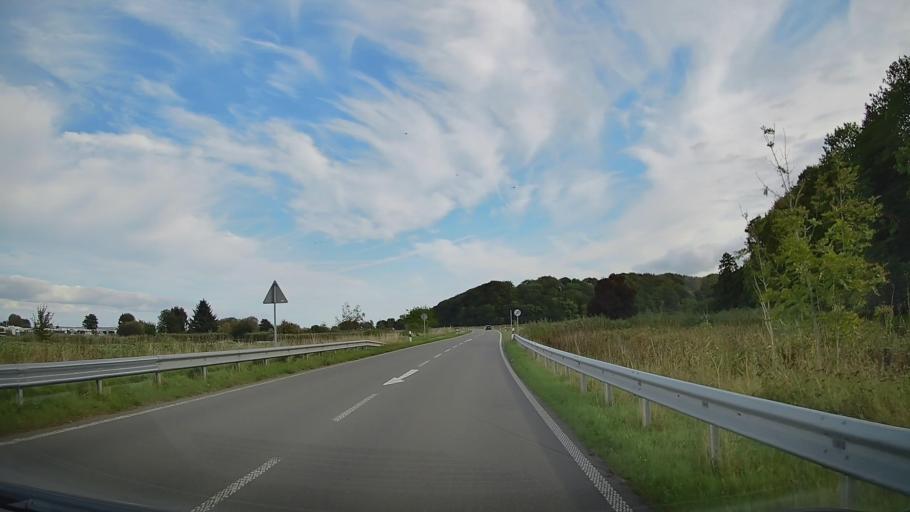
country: DE
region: Schleswig-Holstein
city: Westerholz
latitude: 54.8197
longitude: 9.6563
